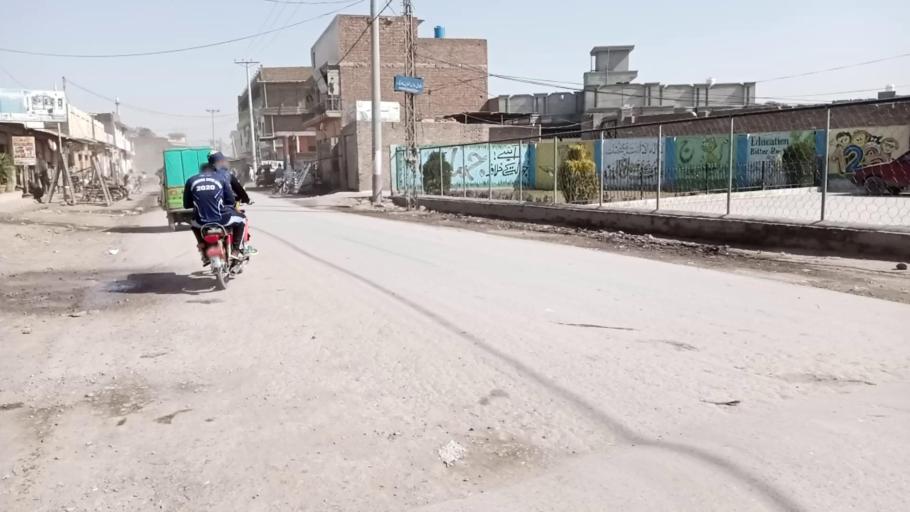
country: PK
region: Khyber Pakhtunkhwa
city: Peshawar
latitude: 34.0055
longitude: 71.6405
